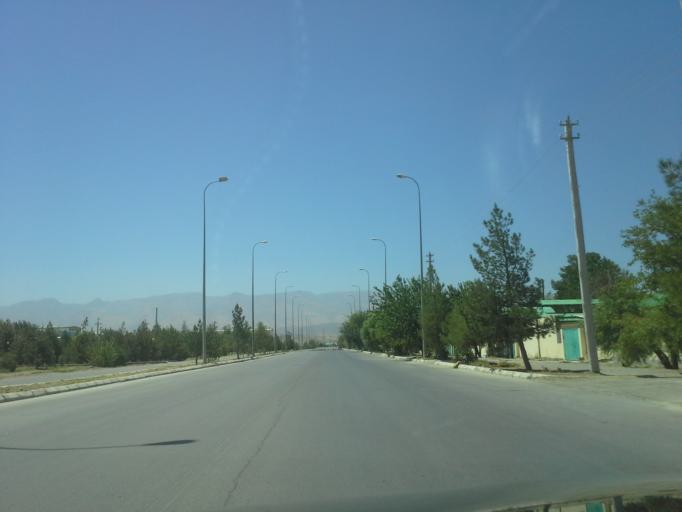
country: TM
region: Ahal
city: Ashgabat
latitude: 38.0062
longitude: 58.3051
